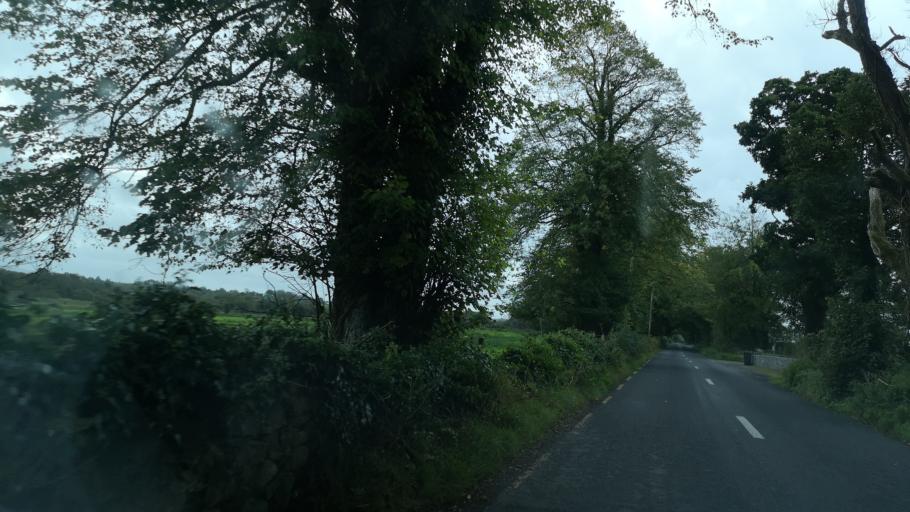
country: IE
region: Connaught
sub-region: County Galway
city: Loughrea
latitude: 53.2845
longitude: -8.6041
